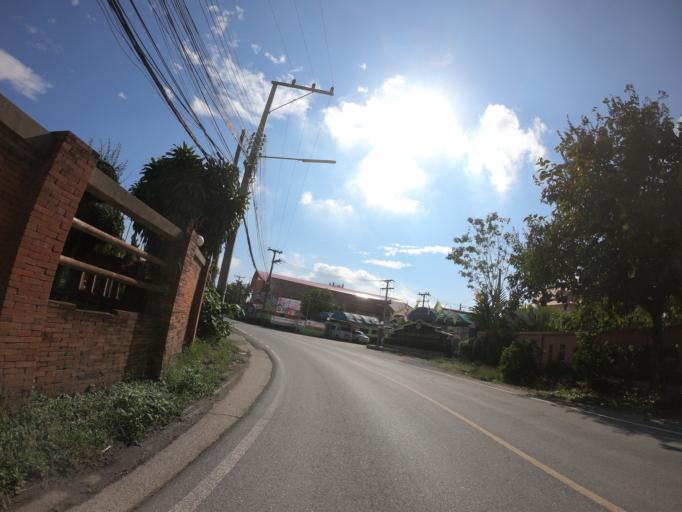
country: TH
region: Chiang Mai
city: San Sai
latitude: 18.8382
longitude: 99.0578
